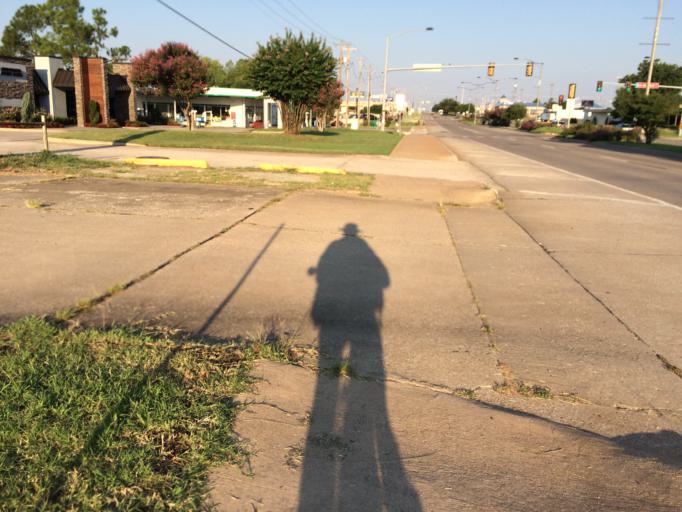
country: US
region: Oklahoma
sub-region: Cleveland County
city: Norman
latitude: 35.2183
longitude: -97.4721
